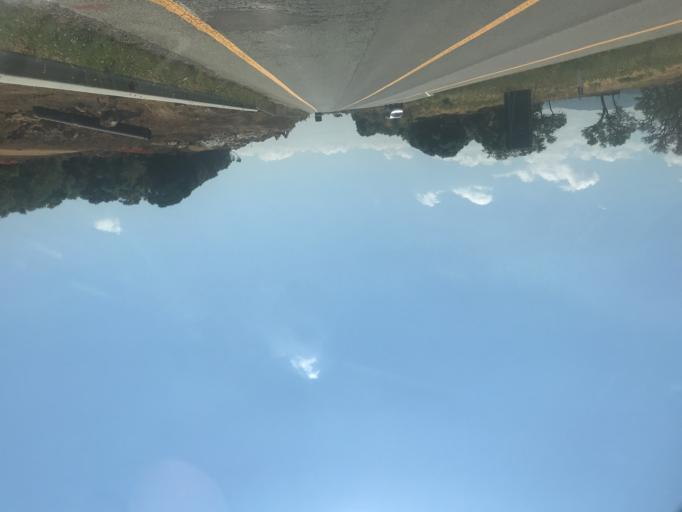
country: IT
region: Sardinia
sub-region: Provincia di Olbia-Tempio
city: Monti
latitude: 40.7937
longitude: 9.2669
